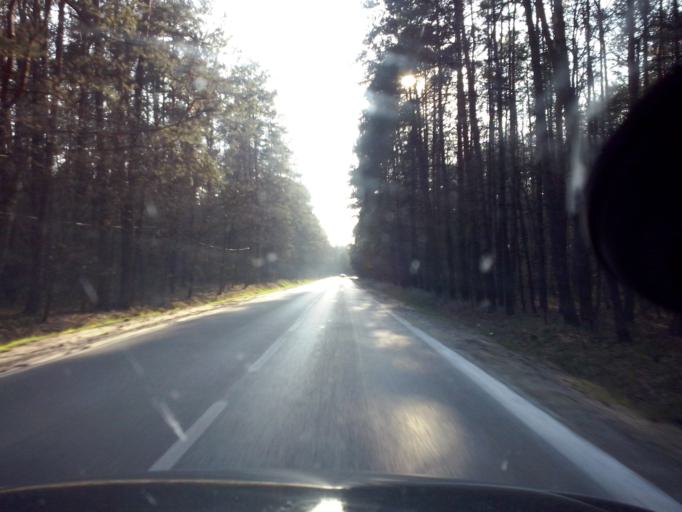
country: PL
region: Lublin Voivodeship
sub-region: Powiat janowski
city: Potok Wielki
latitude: 50.7455
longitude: 22.2202
